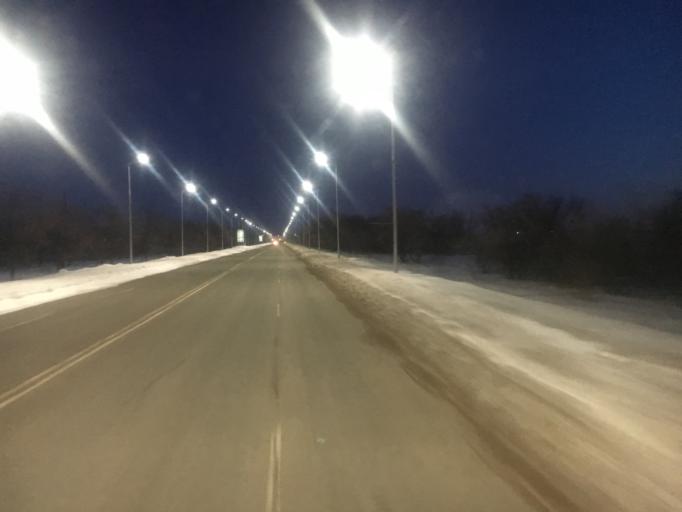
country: KZ
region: Batys Qazaqstan
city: Oral
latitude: 51.1600
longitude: 51.5306
